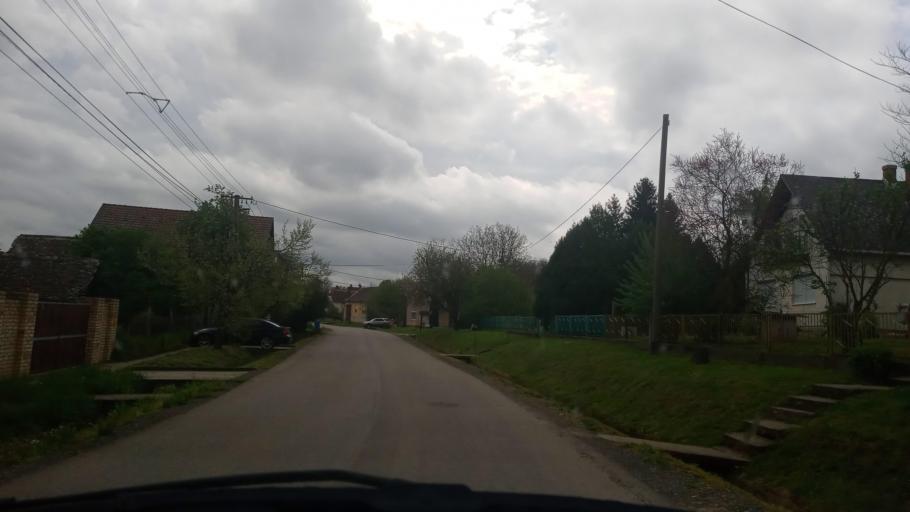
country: HU
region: Baranya
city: Boly
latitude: 45.9768
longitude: 18.4257
